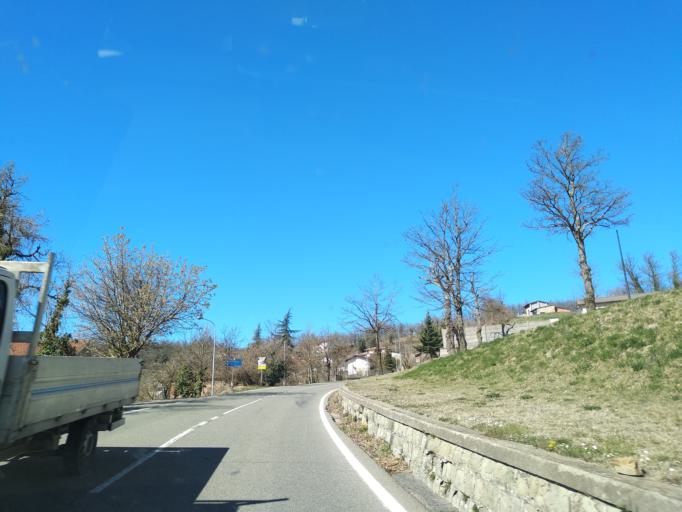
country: IT
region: Emilia-Romagna
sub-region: Provincia di Reggio Emilia
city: Castelnovo ne'Monti
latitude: 44.4179
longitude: 10.3647
